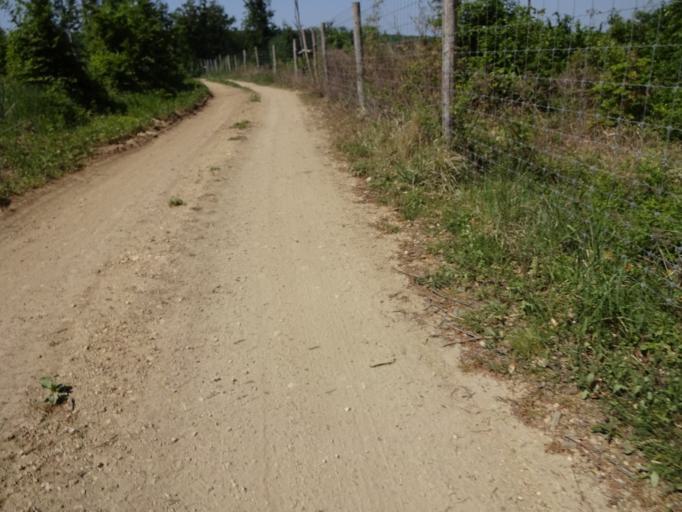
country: HU
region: Veszprem
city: Herend
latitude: 47.1983
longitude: 17.7520
